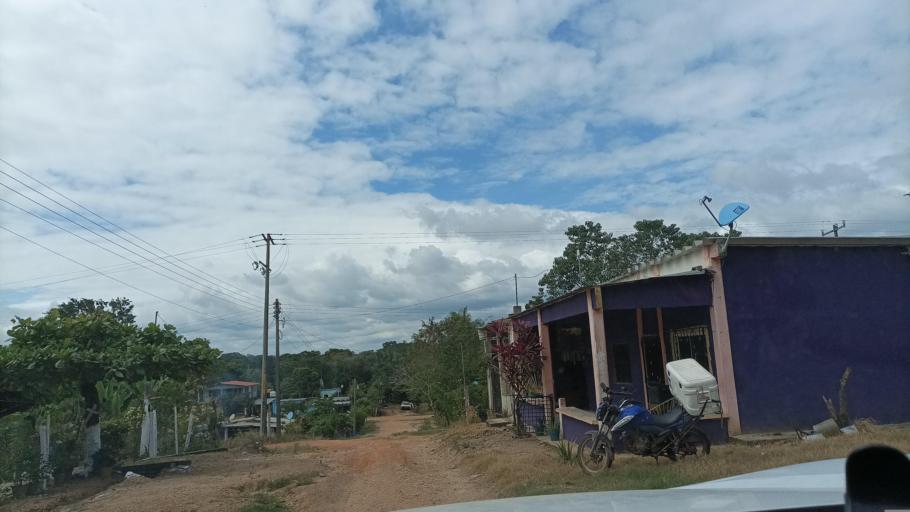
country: MX
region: Veracruz
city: Texistepec
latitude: 17.9610
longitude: -94.8146
